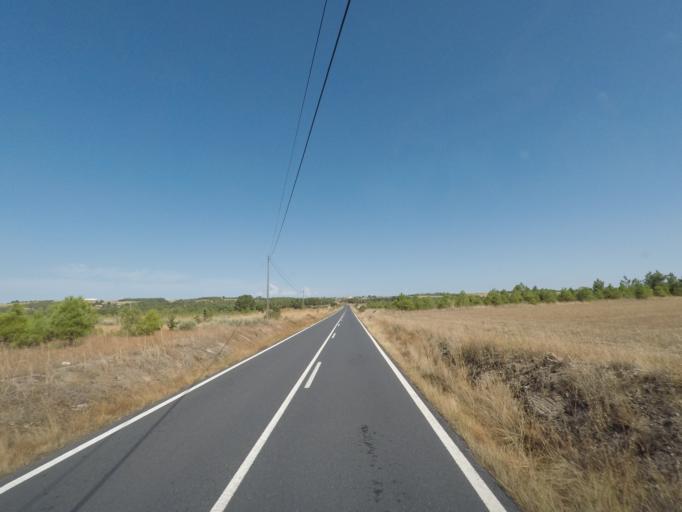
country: ES
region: Castille and Leon
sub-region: Provincia de Salamanca
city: Villarino de los Aires
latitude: 41.3509
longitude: -6.4938
